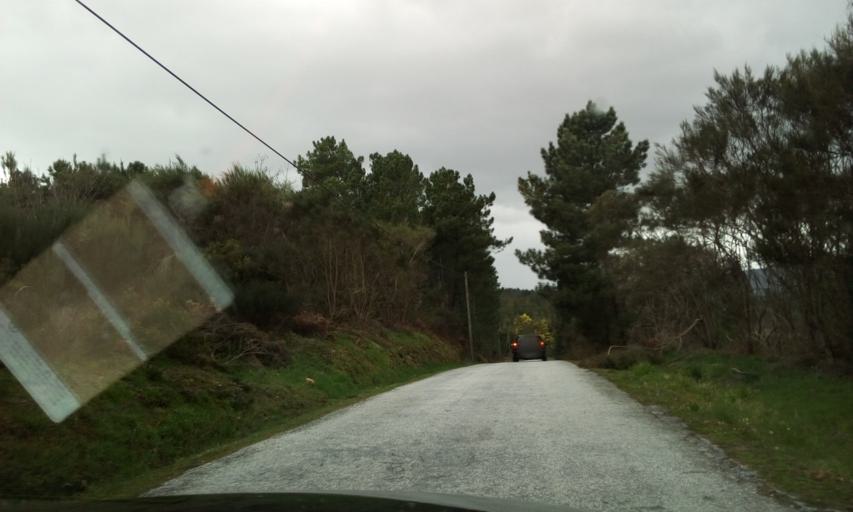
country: PT
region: Guarda
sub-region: Fornos de Algodres
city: Fornos de Algodres
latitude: 40.6367
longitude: -7.5734
